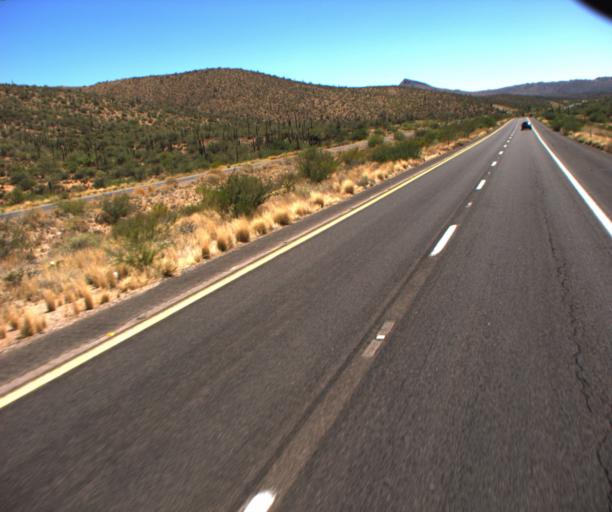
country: US
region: Arizona
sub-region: Maricopa County
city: Rio Verde
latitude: 33.7799
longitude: -111.4932
